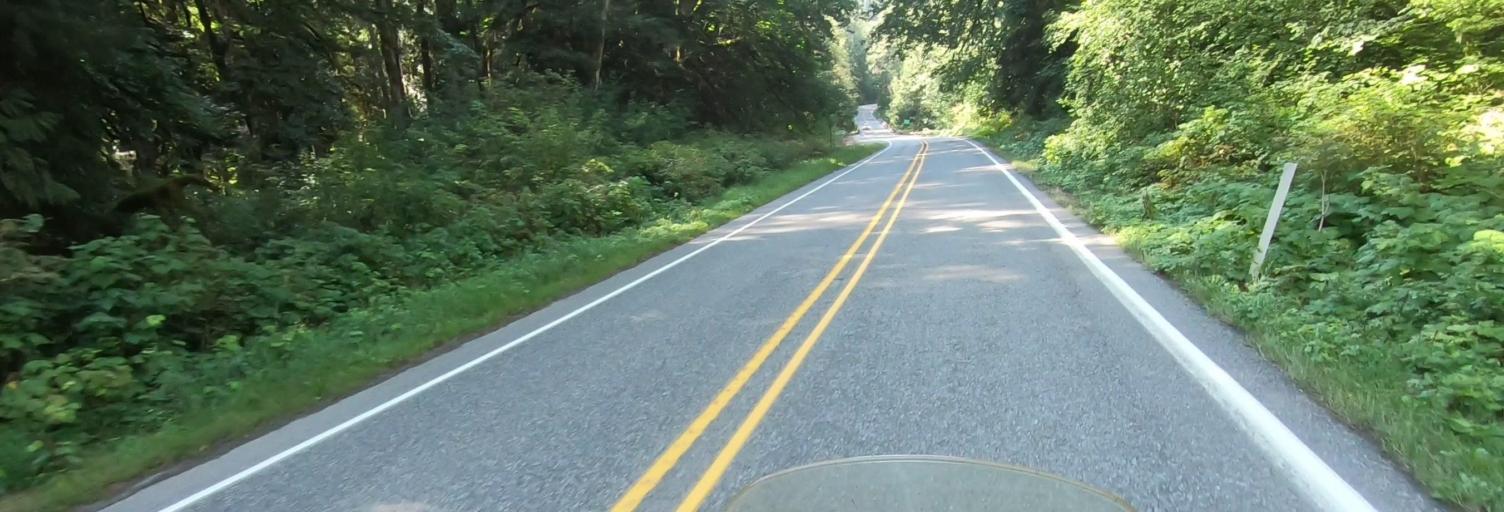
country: US
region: Washington
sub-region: Whatcom County
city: Peaceful Valley
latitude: 48.8999
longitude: -121.9344
